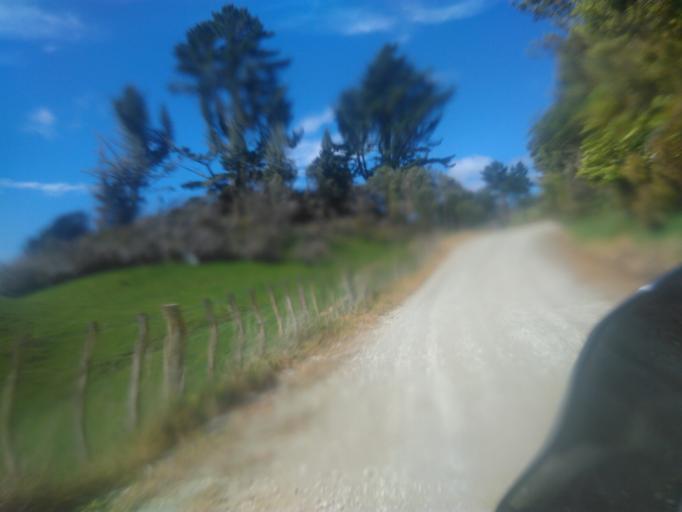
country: NZ
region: Hawke's Bay
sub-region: Wairoa District
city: Wairoa
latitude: -38.7767
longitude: 177.6112
